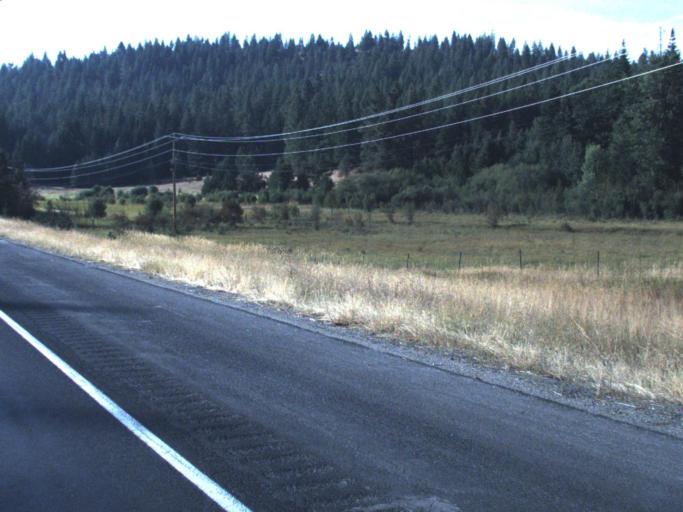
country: US
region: Washington
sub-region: Spokane County
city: Deer Park
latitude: 48.0978
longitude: -117.2938
